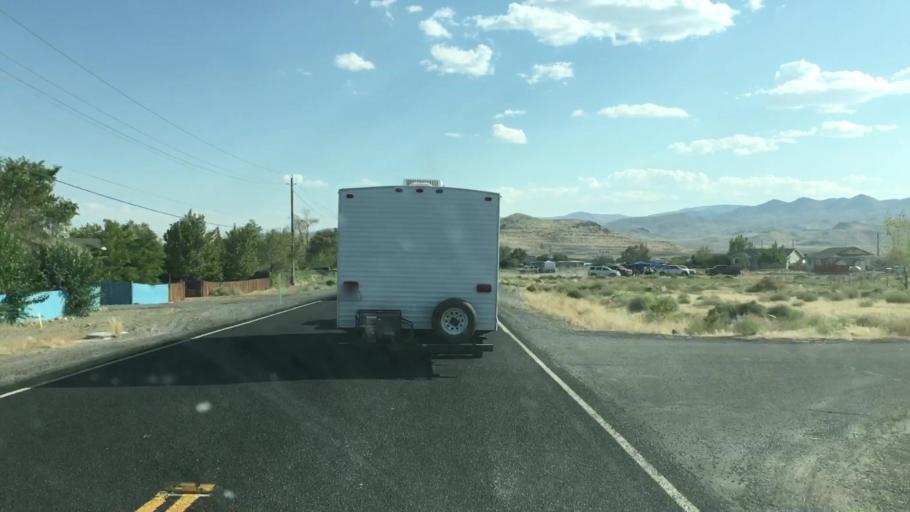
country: US
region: Nevada
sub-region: Lyon County
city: Fernley
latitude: 39.6348
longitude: -119.2906
